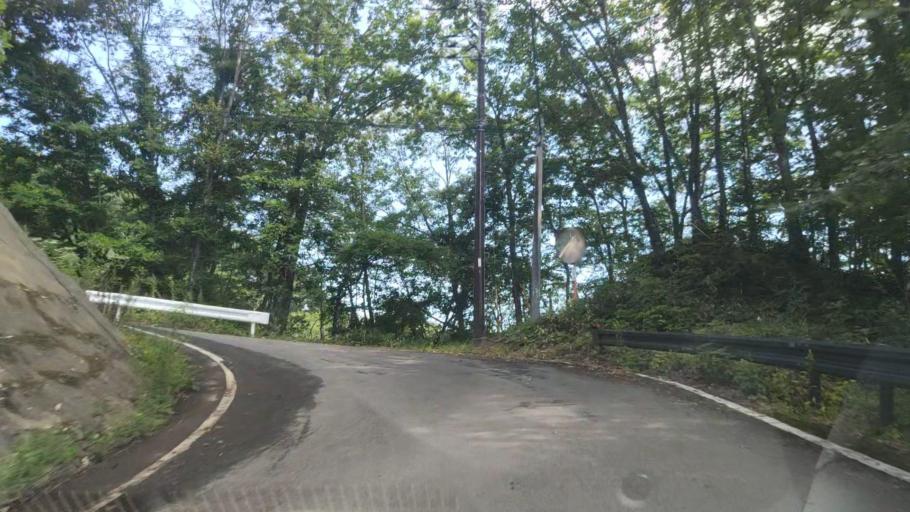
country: JP
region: Gunma
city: Nakanojomachi
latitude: 36.6433
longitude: 138.6125
